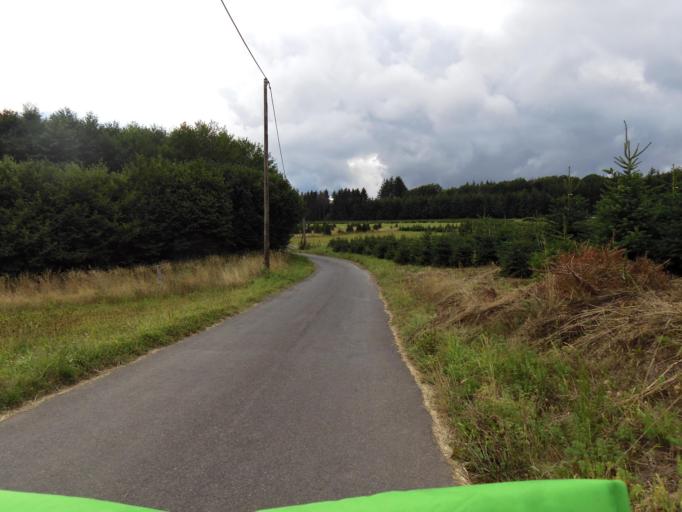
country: BE
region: Wallonia
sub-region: Province de Namur
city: Bievre
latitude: 49.8820
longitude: 4.9943
